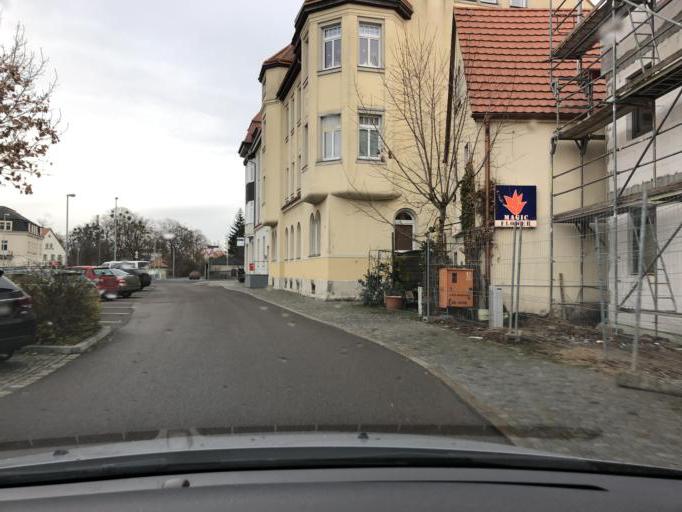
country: DE
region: Saxony
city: Heidenau
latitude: 50.9979
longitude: 13.8213
